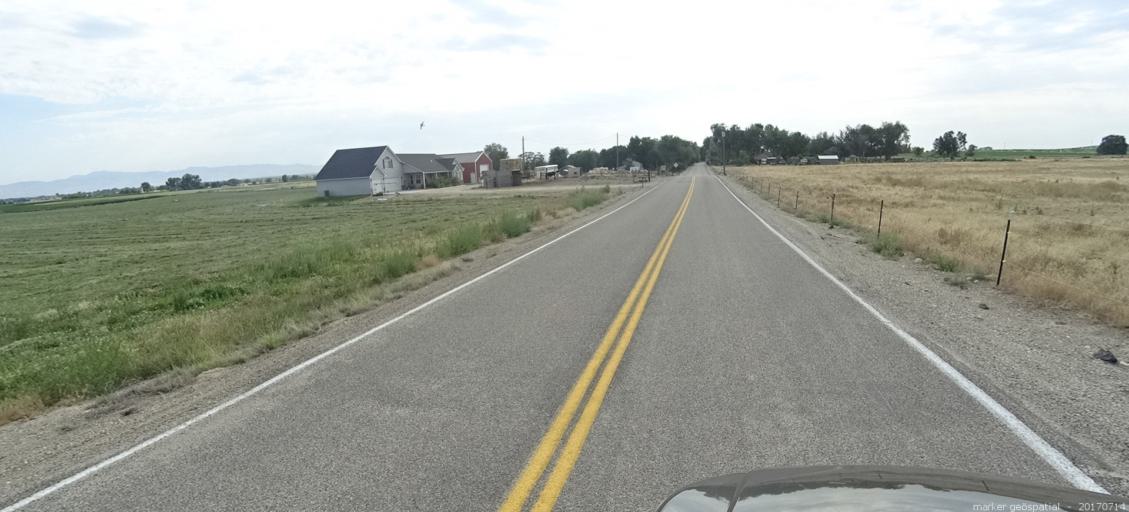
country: US
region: Idaho
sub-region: Ada County
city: Kuna
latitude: 43.4594
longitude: -116.3840
